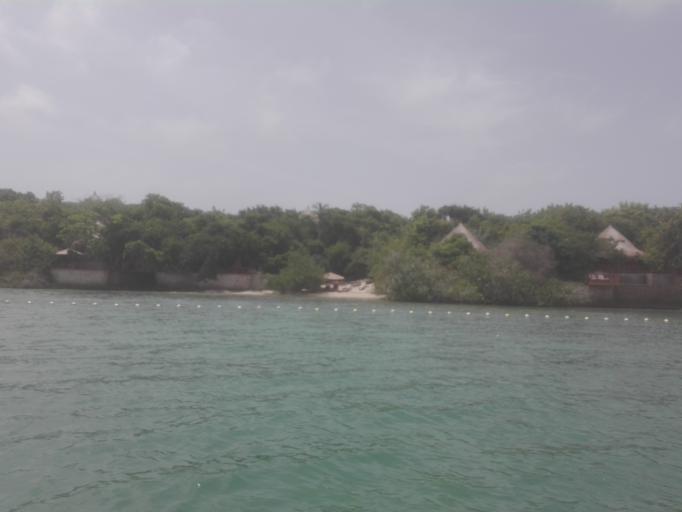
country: CO
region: Bolivar
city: Turbana
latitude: 10.1533
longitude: -75.6868
